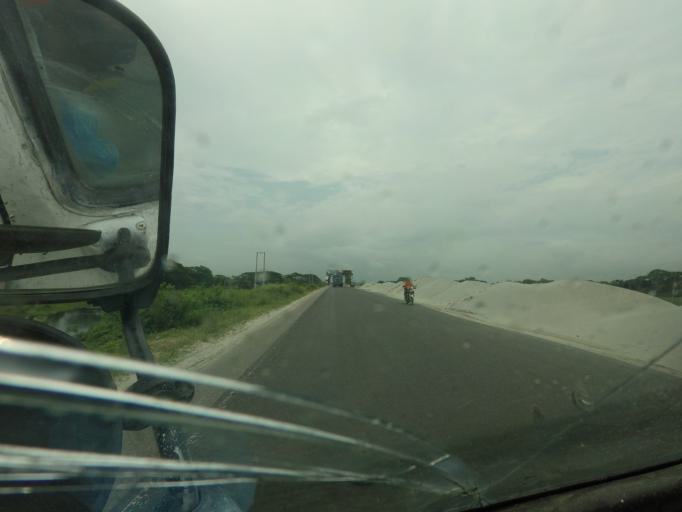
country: BD
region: Dhaka
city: Char Bhadrasan
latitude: 23.3811
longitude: 90.0046
